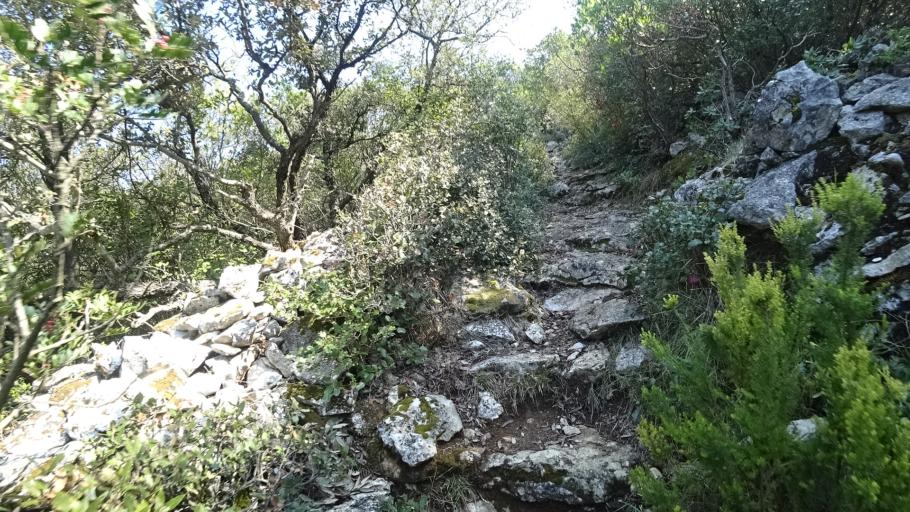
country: HR
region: Primorsko-Goranska
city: Mali Losinj
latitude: 44.4998
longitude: 14.5243
